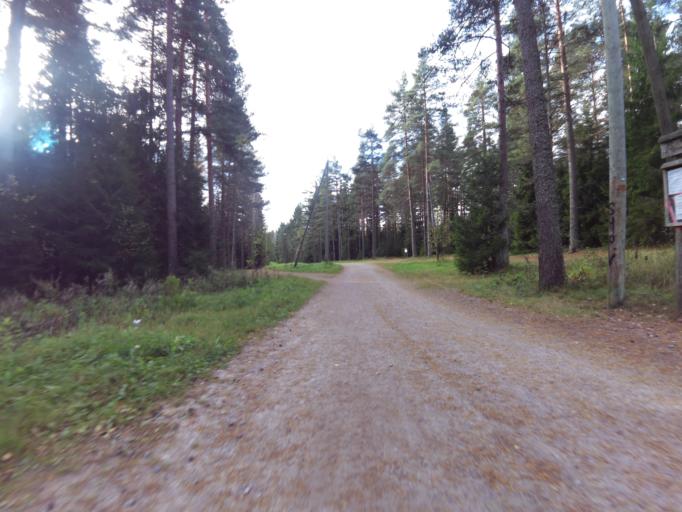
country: FI
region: Uusimaa
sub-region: Helsinki
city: Kauniainen
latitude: 60.1875
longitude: 24.6939
